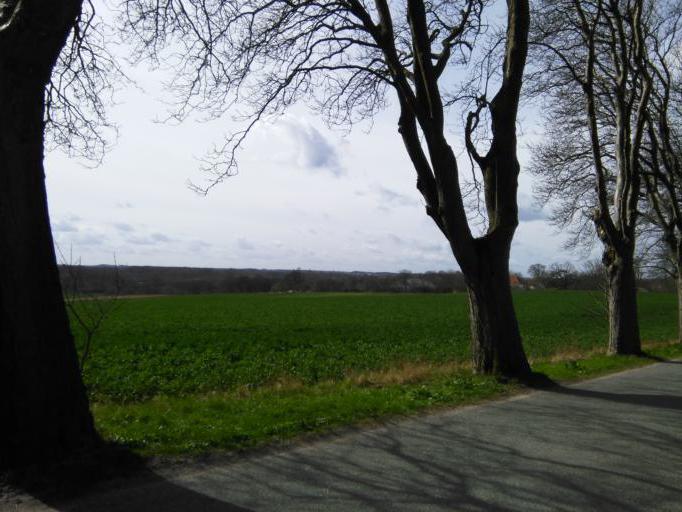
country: DK
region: Central Jutland
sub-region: Arhus Kommune
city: Beder
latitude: 56.0853
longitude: 10.2178
